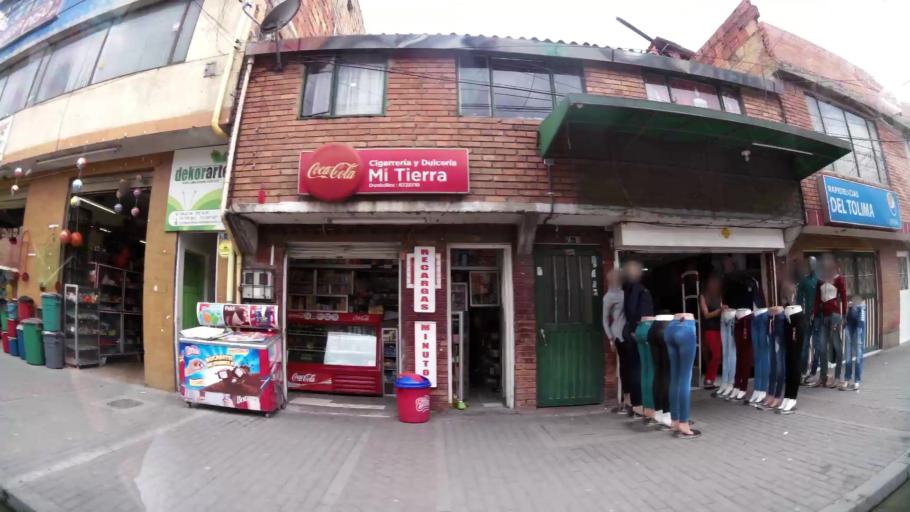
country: CO
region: Cundinamarca
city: Cota
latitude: 4.7650
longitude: -74.0347
